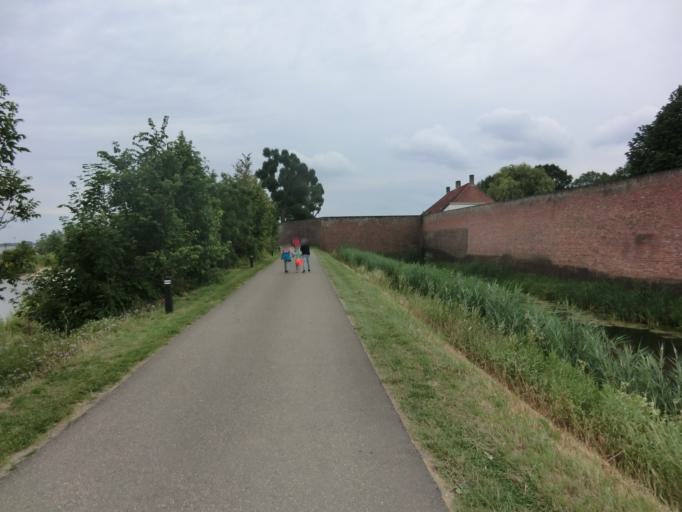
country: NL
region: North Brabant
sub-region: Gemeente Woudrichem
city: Woudrichem
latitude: 51.8175
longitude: 5.0215
